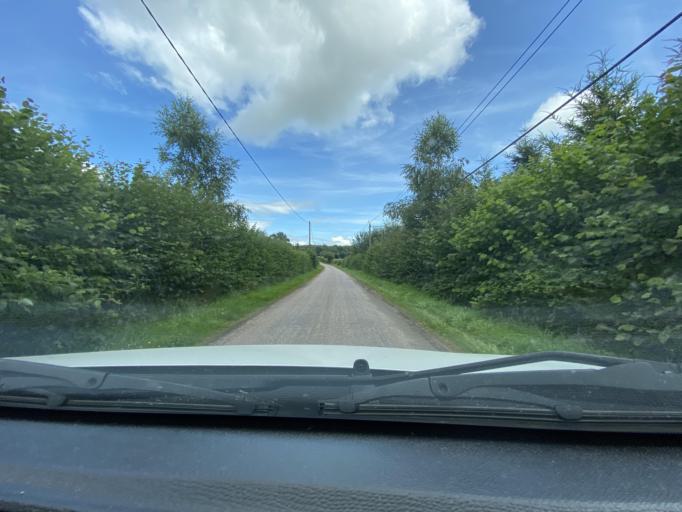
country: FR
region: Bourgogne
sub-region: Departement de la Cote-d'Or
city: Saulieu
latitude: 47.2644
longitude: 4.1990
